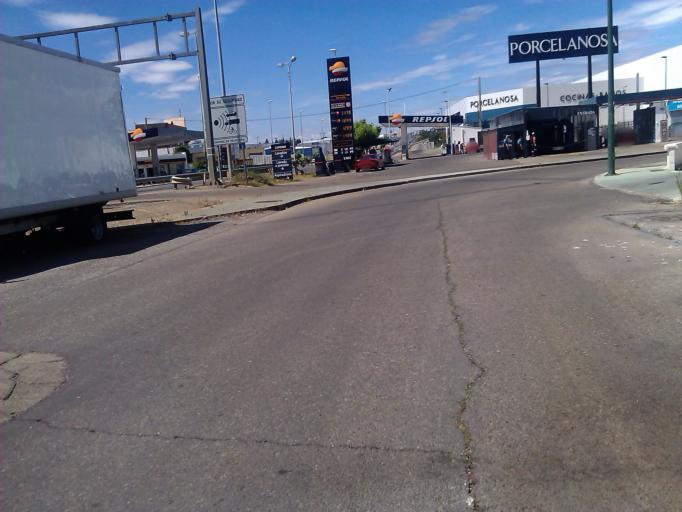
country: ES
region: Castille and Leon
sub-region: Provincia de Leon
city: San Andres del Rabanedo
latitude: 42.5912
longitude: -5.6150
